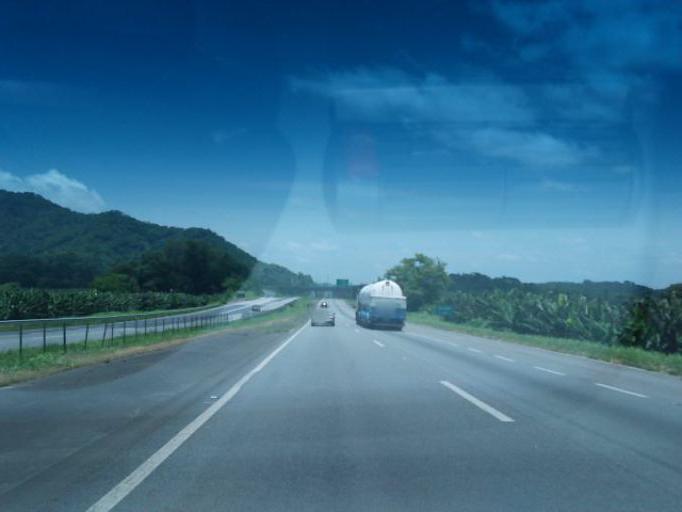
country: BR
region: Sao Paulo
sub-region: Miracatu
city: Miracatu
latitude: -24.3117
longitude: -47.5138
